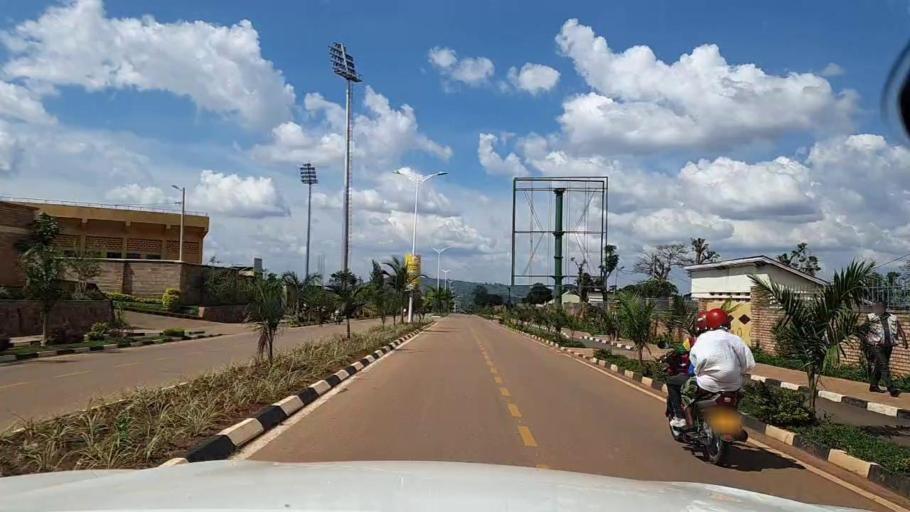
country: RW
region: Southern Province
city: Butare
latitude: -2.5982
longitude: 29.7424
